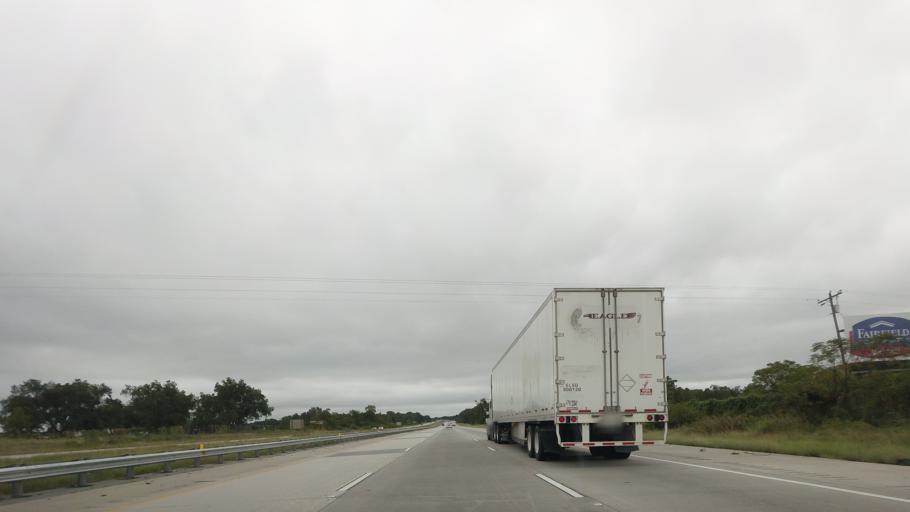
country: US
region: Georgia
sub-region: Dooly County
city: Unadilla
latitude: 32.2342
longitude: -83.7411
